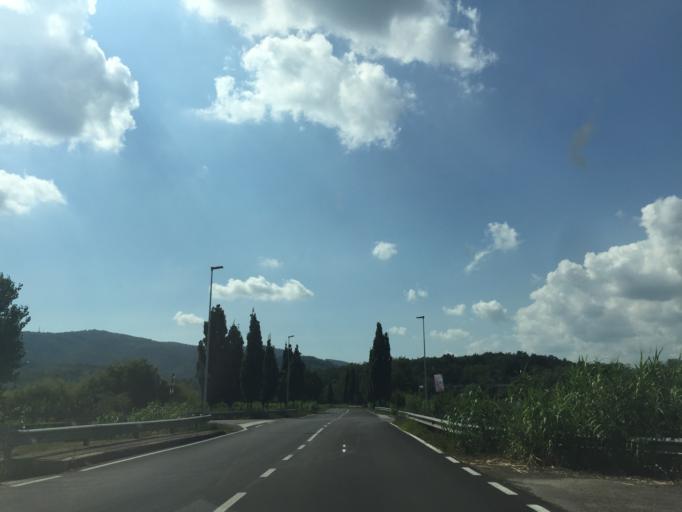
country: IT
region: Tuscany
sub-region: Provincia di Pistoia
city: Cantagrillo-Casalguidi
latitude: 43.8863
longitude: 10.9025
